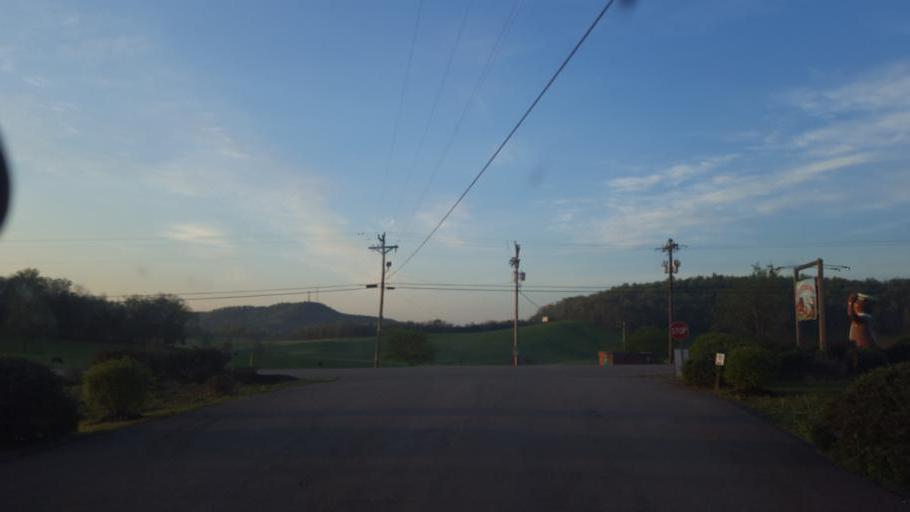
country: US
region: Kentucky
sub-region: Barren County
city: Cave City
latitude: 37.1351
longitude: -85.9953
